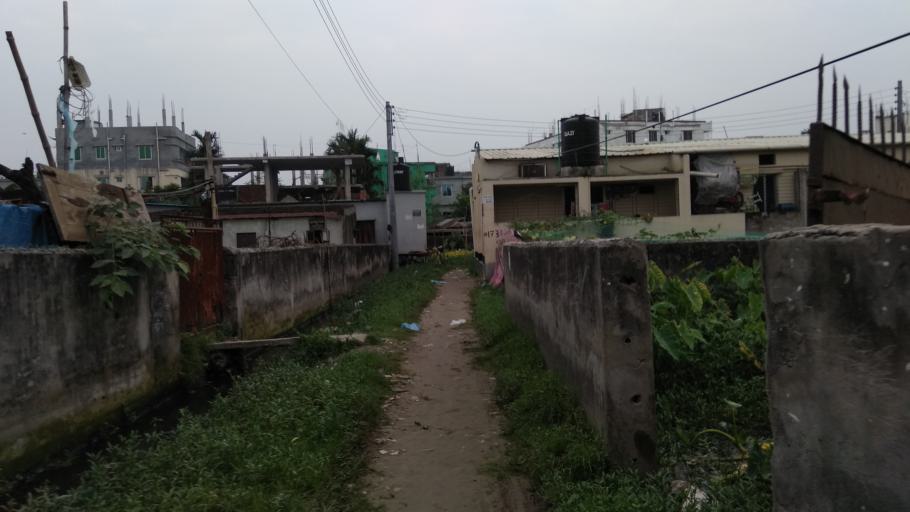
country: BD
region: Dhaka
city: Tungi
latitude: 23.8563
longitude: 90.4290
